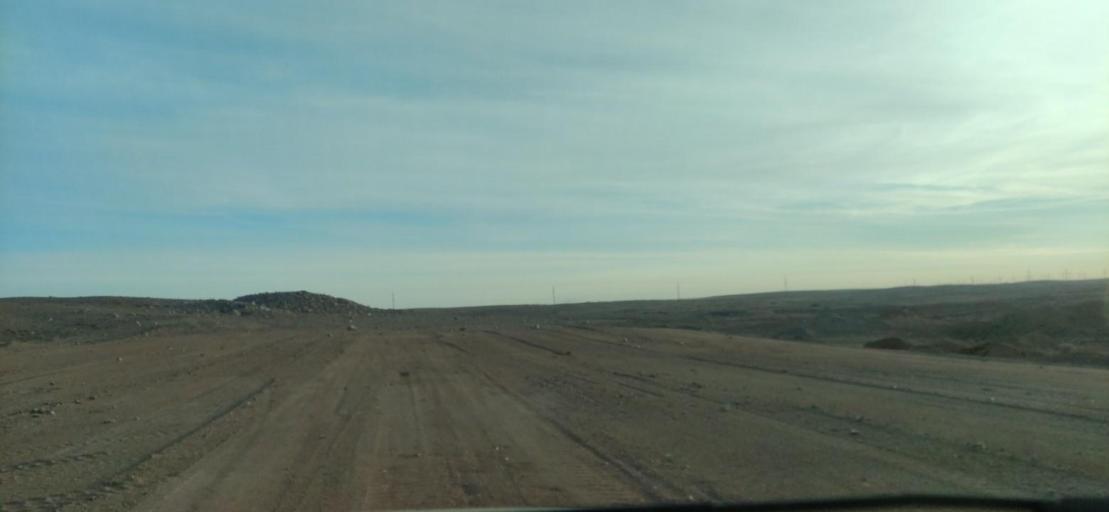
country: KZ
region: Qaraghandy
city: Saryshaghan
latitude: 46.1113
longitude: 73.5957
